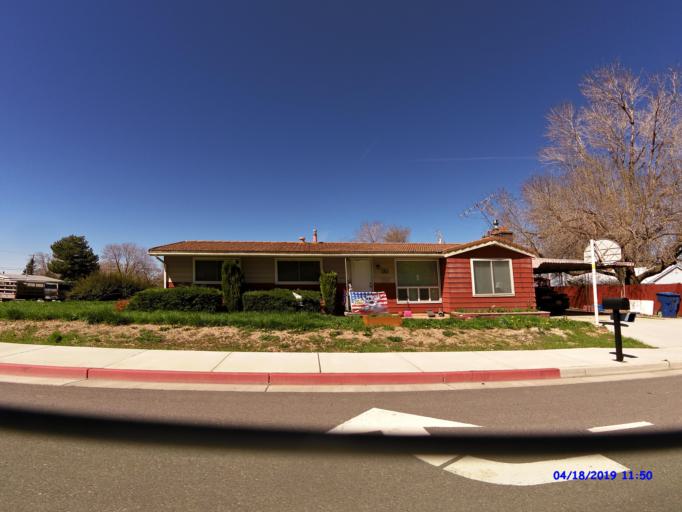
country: US
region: Utah
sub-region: Weber County
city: Harrisville
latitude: 41.2629
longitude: -111.9479
